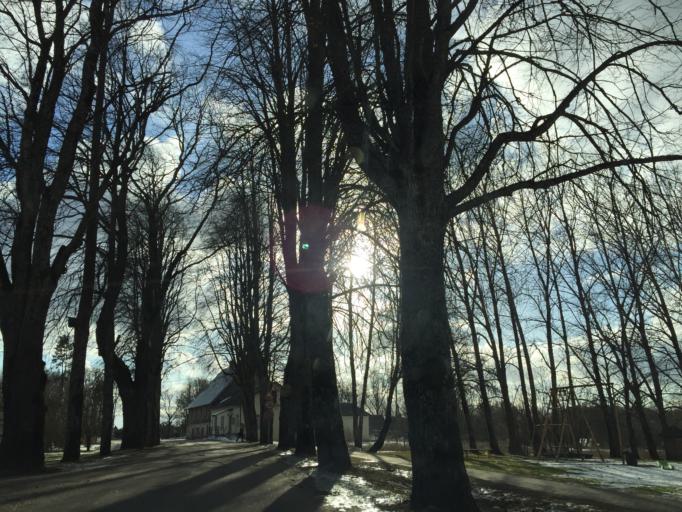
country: LV
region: Limbazu Rajons
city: Limbazi
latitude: 57.6100
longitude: 24.6082
